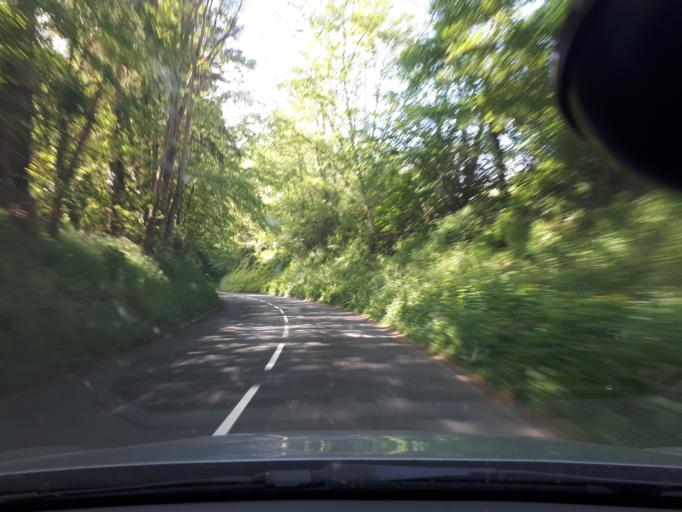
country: FR
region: Pays de la Loire
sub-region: Departement de la Sarthe
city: Change
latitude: 48.0254
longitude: 0.2773
